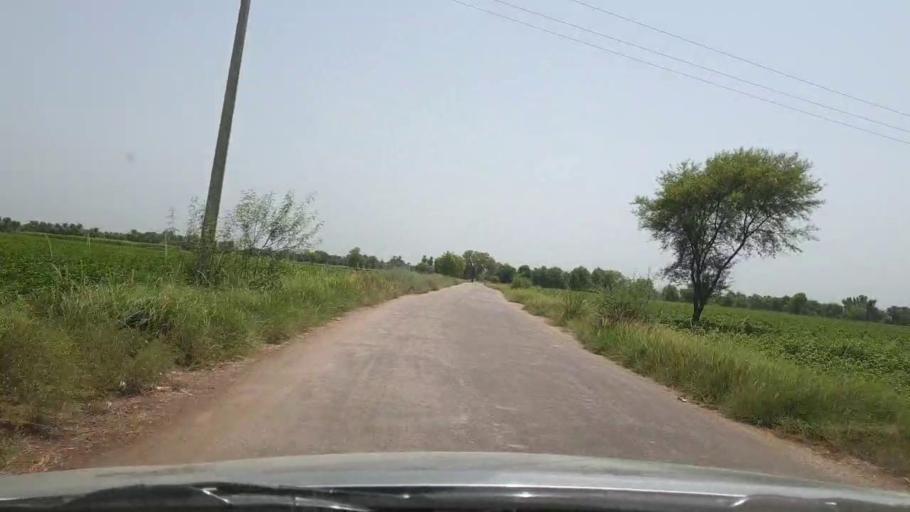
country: PK
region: Sindh
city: Pano Aqil
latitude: 27.8808
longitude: 69.1465
